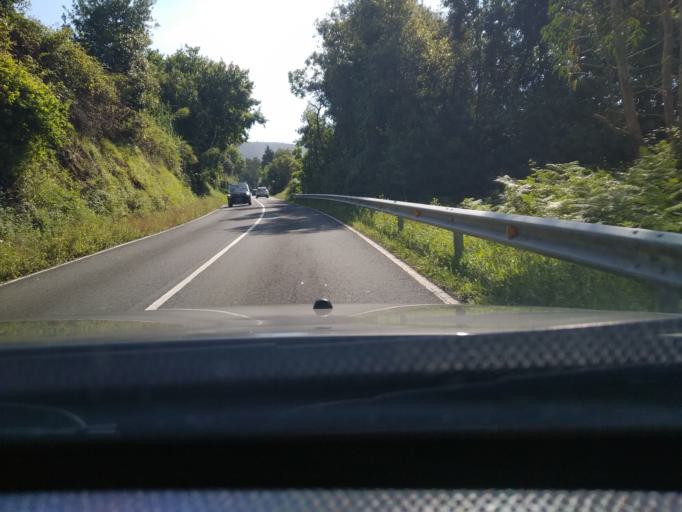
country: ES
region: Basque Country
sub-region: Bizkaia
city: Bakio
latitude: 43.4335
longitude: -2.7885
